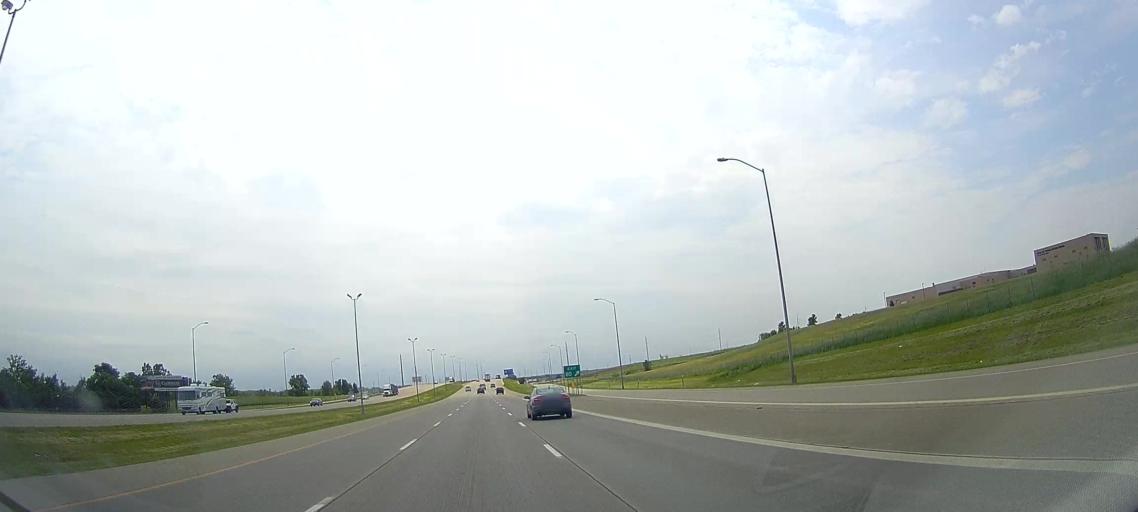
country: US
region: South Dakota
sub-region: Minnehaha County
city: Sioux Falls
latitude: 43.5630
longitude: -96.7791
